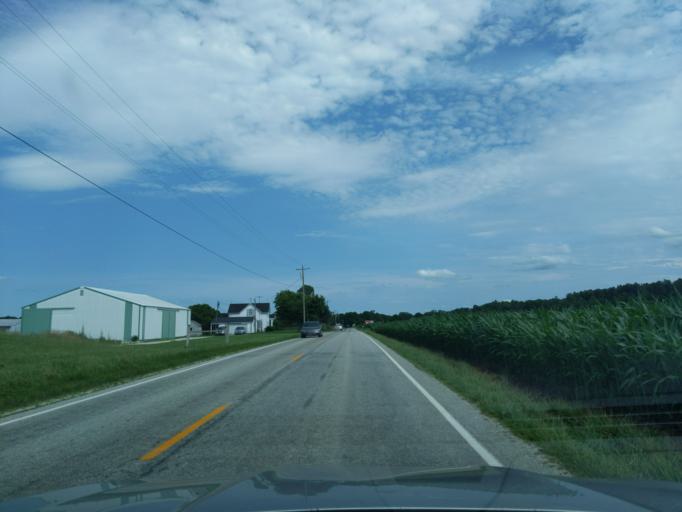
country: US
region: Indiana
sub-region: Ripley County
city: Osgood
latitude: 39.2009
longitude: -85.3092
